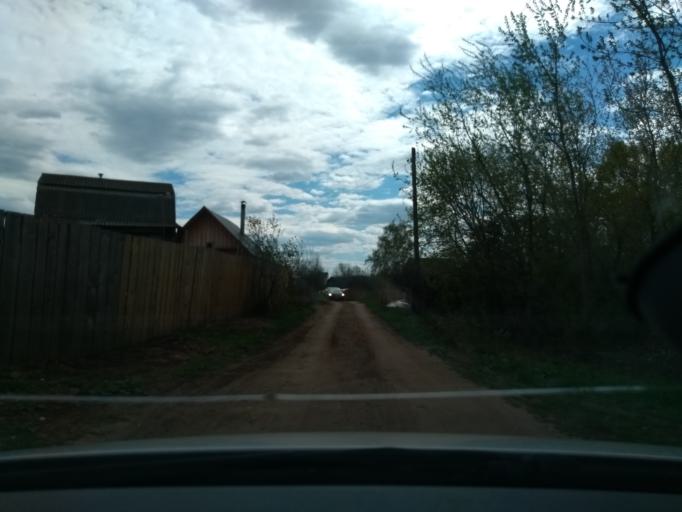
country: RU
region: Perm
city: Lobanovo
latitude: 57.8693
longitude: 56.3038
